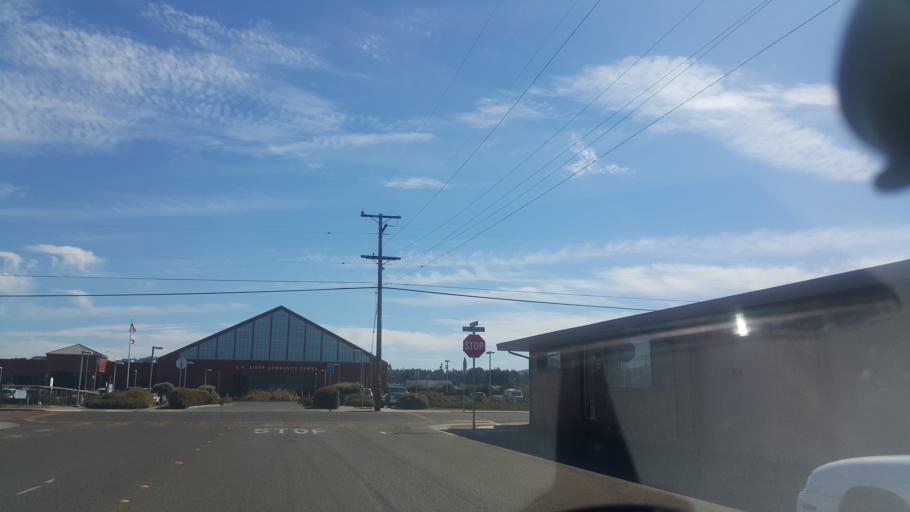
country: US
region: California
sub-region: Mendocino County
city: Fort Bragg
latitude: 39.4391
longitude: -123.7960
